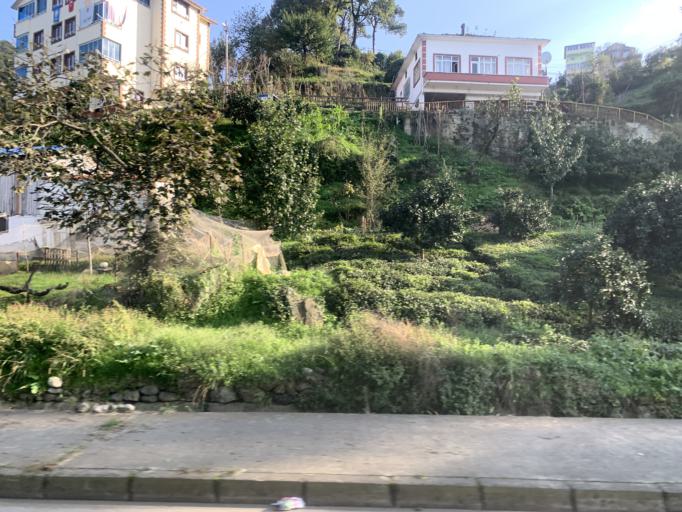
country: TR
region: Trabzon
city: Of
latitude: 40.9292
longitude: 40.2339
